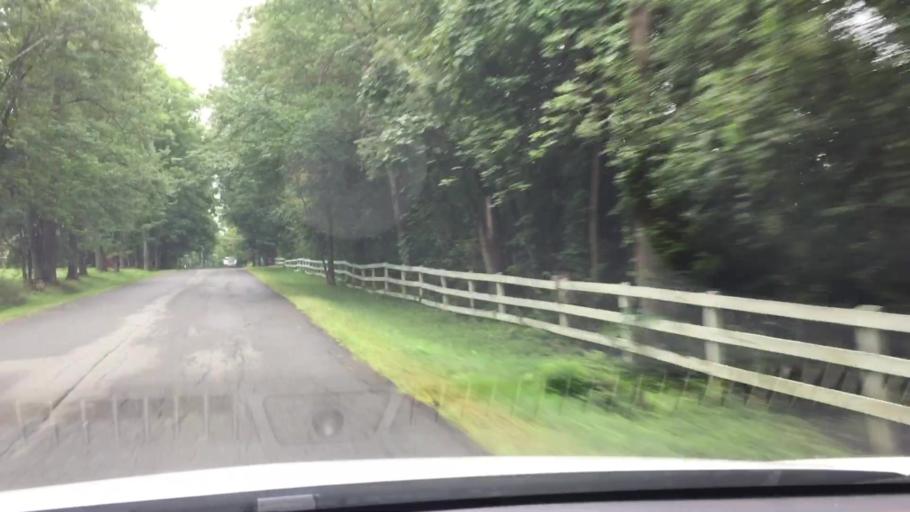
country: US
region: Massachusetts
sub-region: Berkshire County
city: Richmond
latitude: 42.3974
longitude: -73.3541
